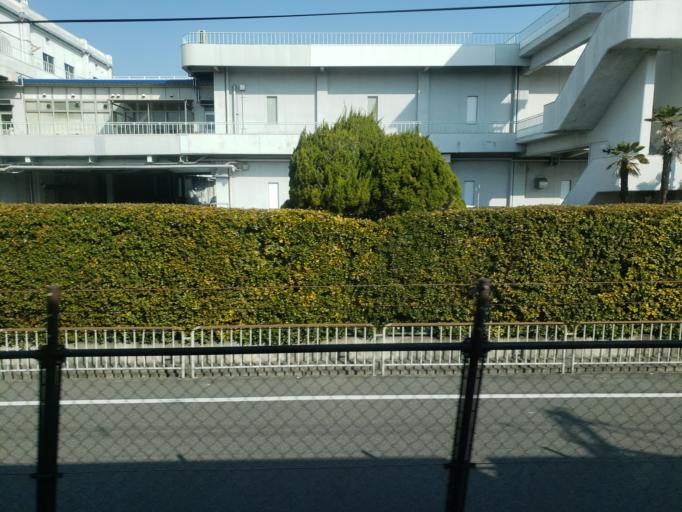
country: JP
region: Hyogo
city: Nishinomiya-hama
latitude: 34.7392
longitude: 135.3633
